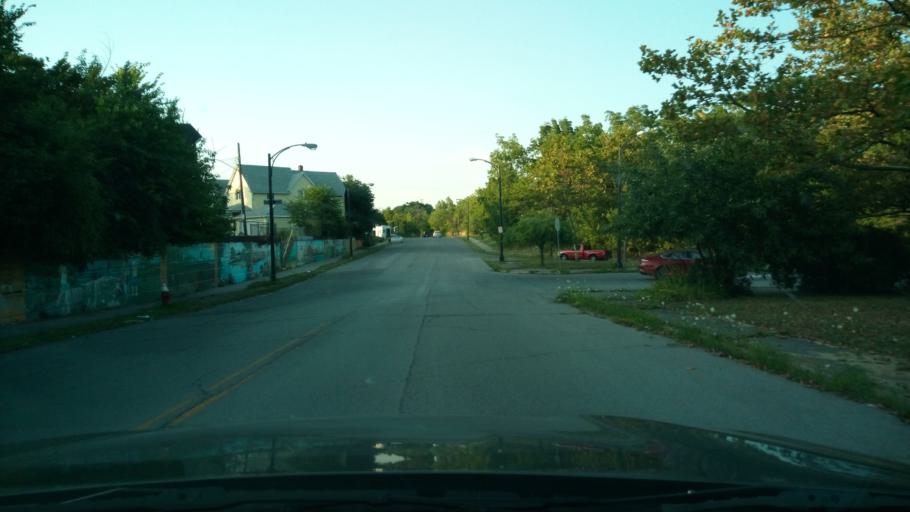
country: US
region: New York
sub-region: Erie County
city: Kenmore
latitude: 42.9358
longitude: -78.8991
